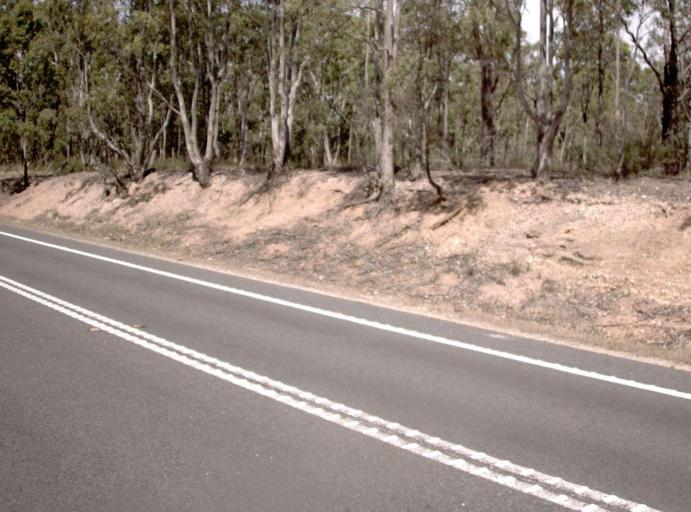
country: AU
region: Victoria
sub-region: Wellington
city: Sale
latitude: -37.9449
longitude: 147.1251
